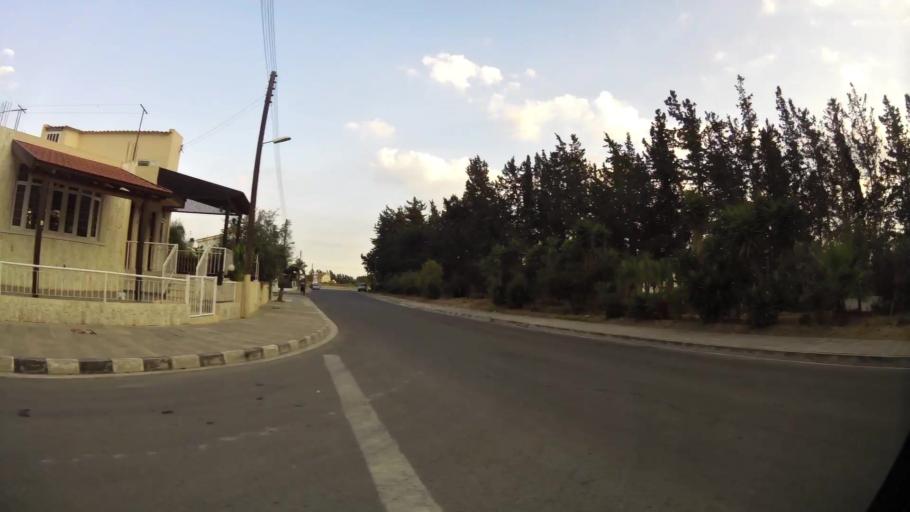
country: CY
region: Larnaka
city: Meneou
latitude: 34.8605
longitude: 33.5890
